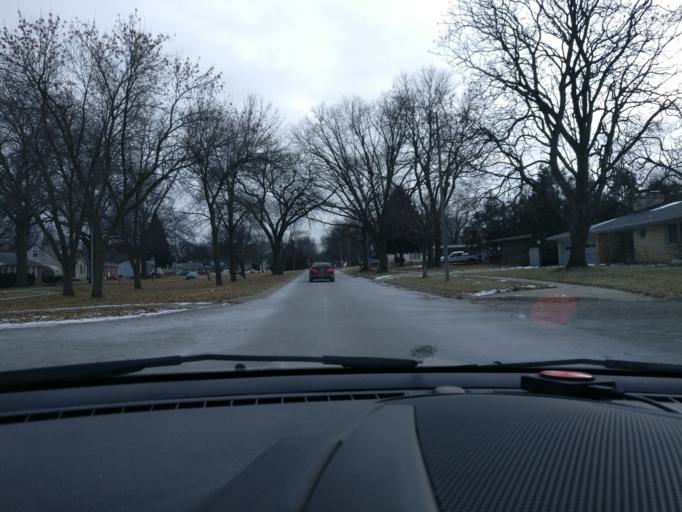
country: US
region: Nebraska
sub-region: Lancaster County
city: Lincoln
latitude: 40.8447
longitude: -96.6402
